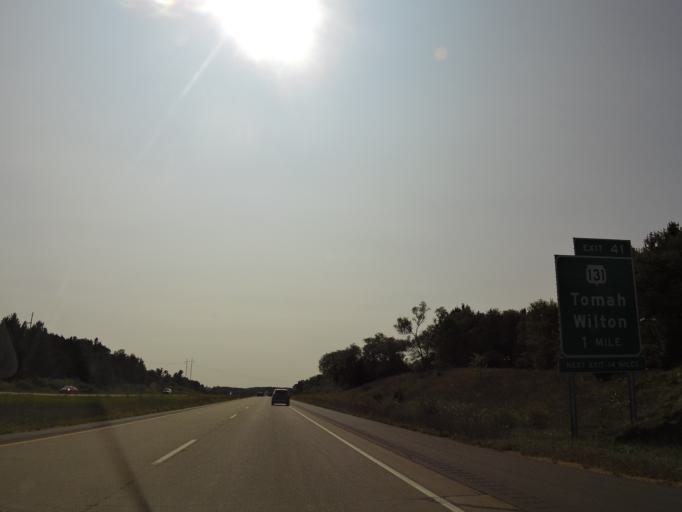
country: US
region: Wisconsin
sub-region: Monroe County
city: Tomah
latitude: 43.9680
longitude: -90.4828
